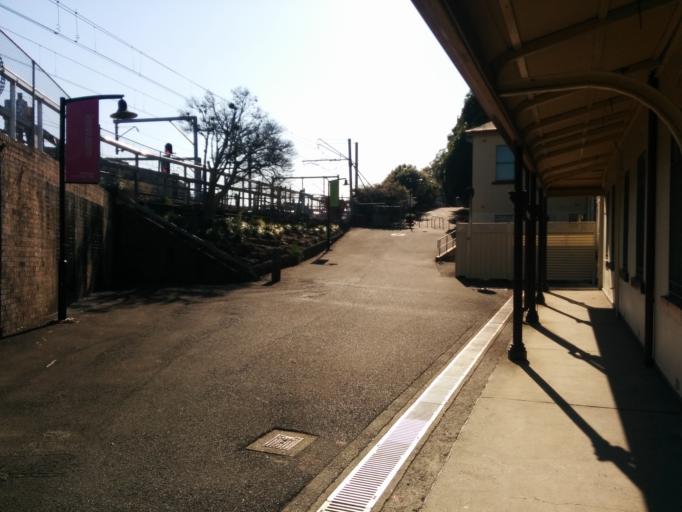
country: AU
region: New South Wales
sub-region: City of Sydney
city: Darlington
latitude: -33.8935
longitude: 151.1967
